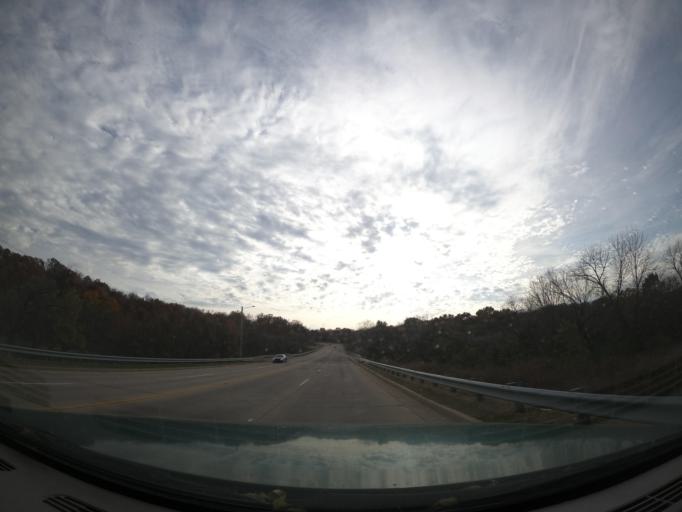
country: US
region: Oklahoma
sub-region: Tulsa County
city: Turley
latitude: 36.2160
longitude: -95.9948
